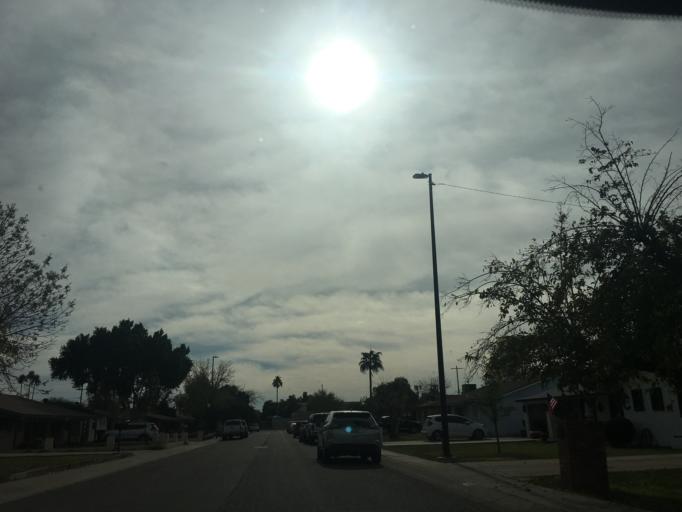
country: US
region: Arizona
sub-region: Maricopa County
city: Gilbert
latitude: 33.3477
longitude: -111.7944
